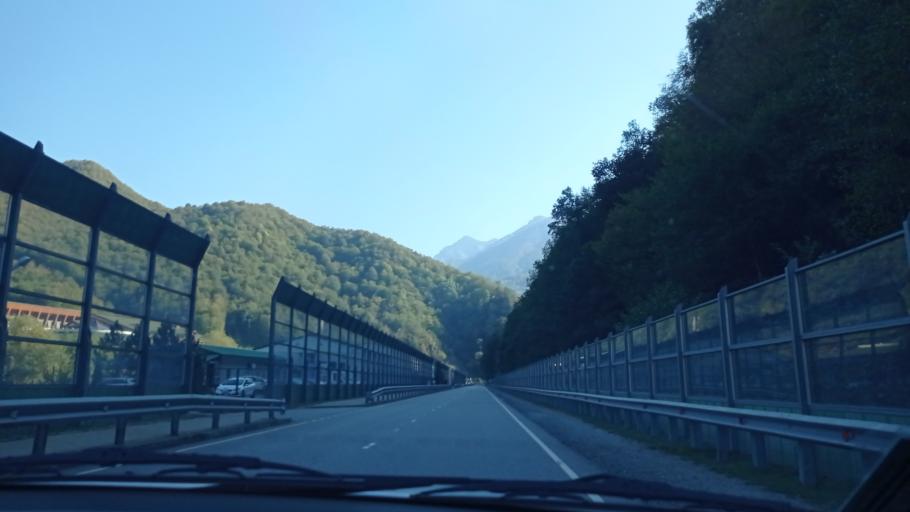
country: RU
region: Krasnodarskiy
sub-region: Sochi City
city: Krasnaya Polyana
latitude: 43.6880
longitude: 40.2750
